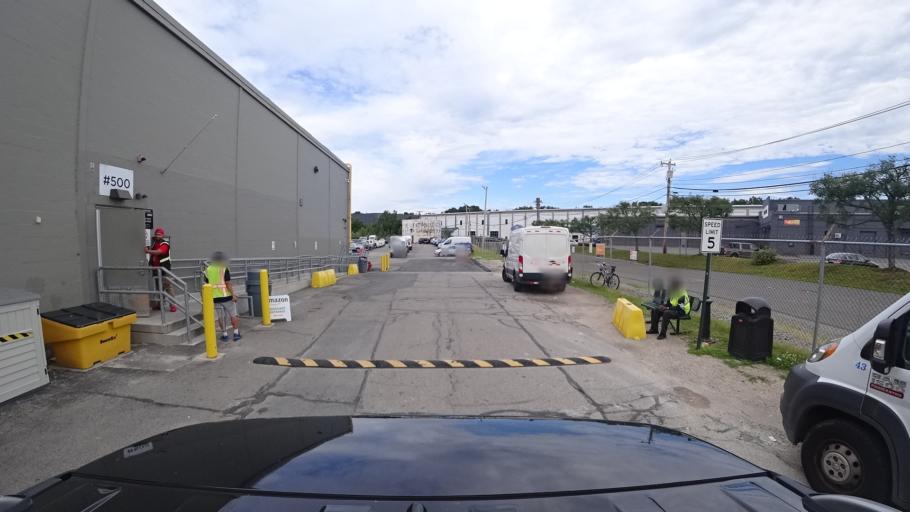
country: US
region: Massachusetts
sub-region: Norfolk County
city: Dedham
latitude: 42.2342
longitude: -71.1404
